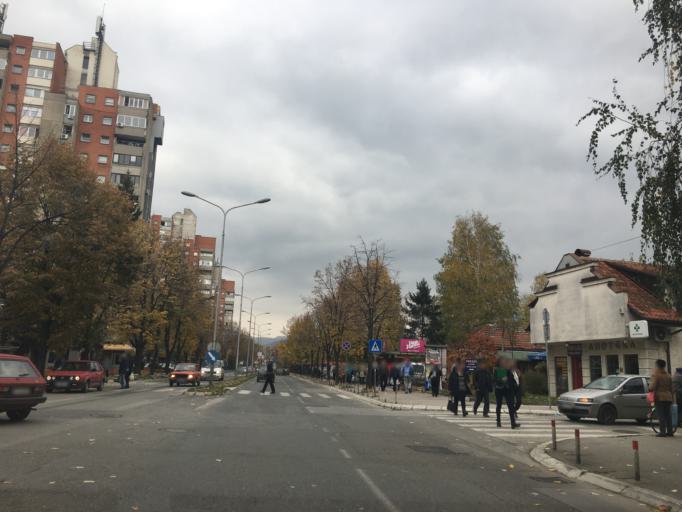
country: RS
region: Central Serbia
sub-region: Raski Okrug
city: Kraljevo
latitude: 43.7228
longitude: 20.6932
